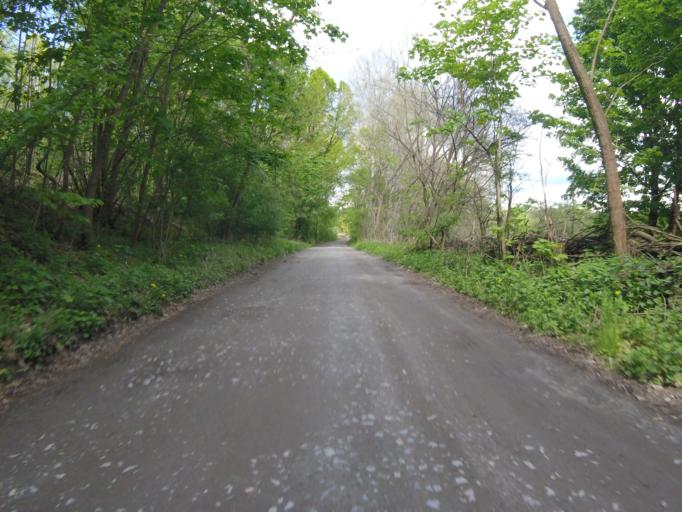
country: DE
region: Brandenburg
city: Teupitz
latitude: 52.1249
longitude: 13.5952
